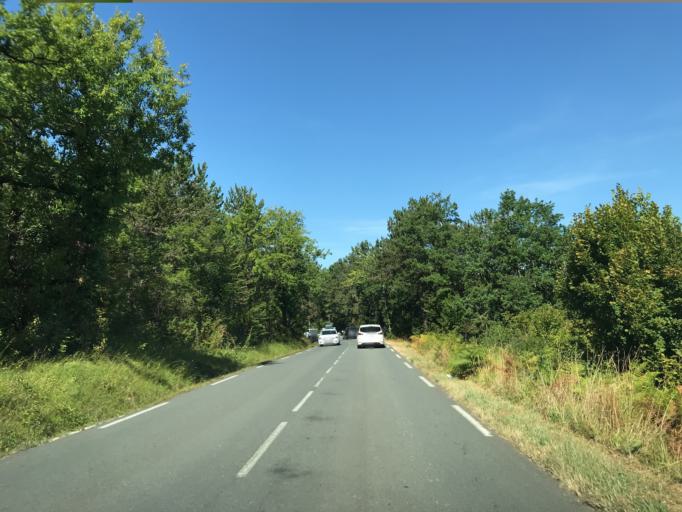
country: FR
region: Limousin
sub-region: Departement de la Correze
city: Larche
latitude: 45.1011
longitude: 1.3926
